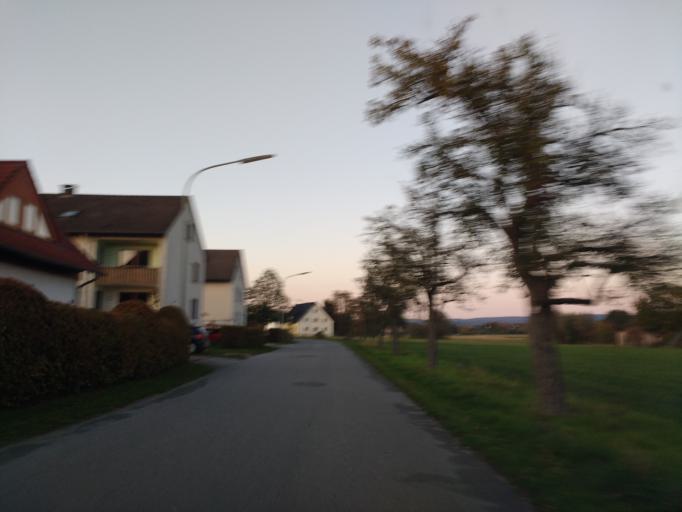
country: DE
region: North Rhine-Westphalia
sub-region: Regierungsbezirk Detmold
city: Schlangen
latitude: 51.8014
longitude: 8.8425
